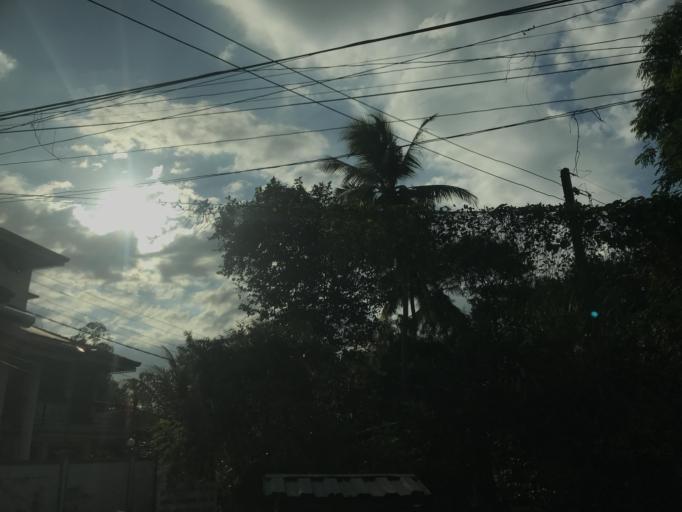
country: LK
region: Western
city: Gampaha
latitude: 7.0669
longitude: 80.0047
